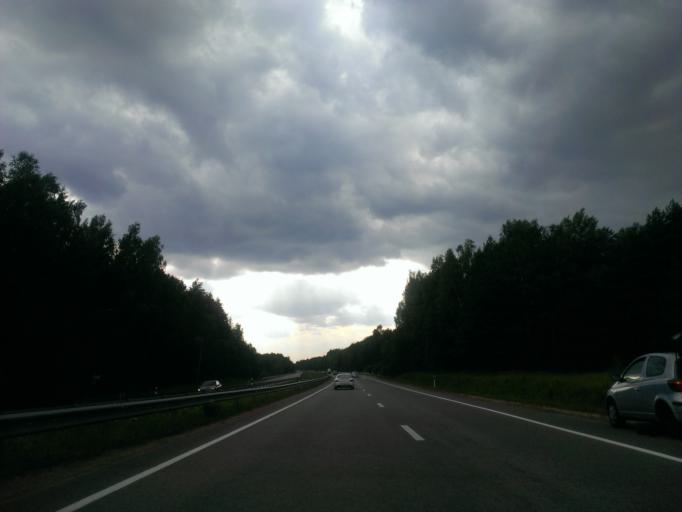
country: LV
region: Krimulda
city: Ragana
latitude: 57.1347
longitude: 24.7768
